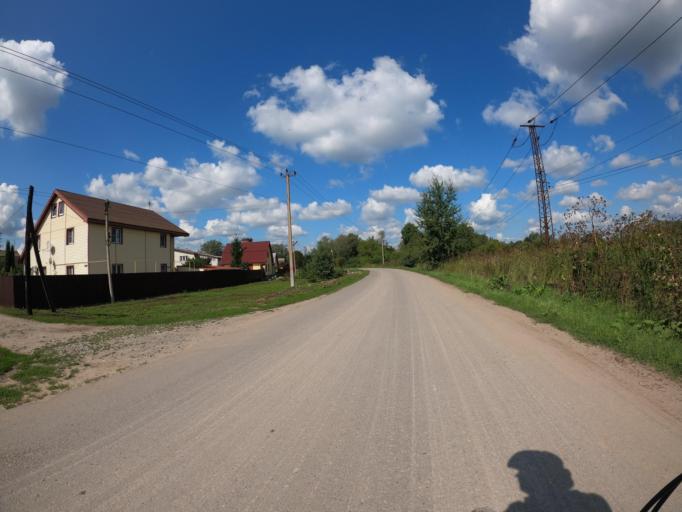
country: RU
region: Moskovskaya
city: Lopatinskiy
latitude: 55.3143
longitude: 38.7054
